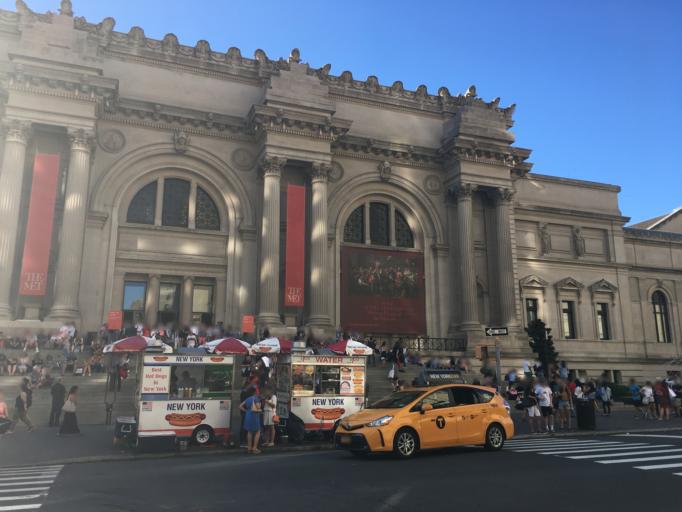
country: US
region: New York
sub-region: New York County
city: Manhattan
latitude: 40.7790
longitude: -73.9623
